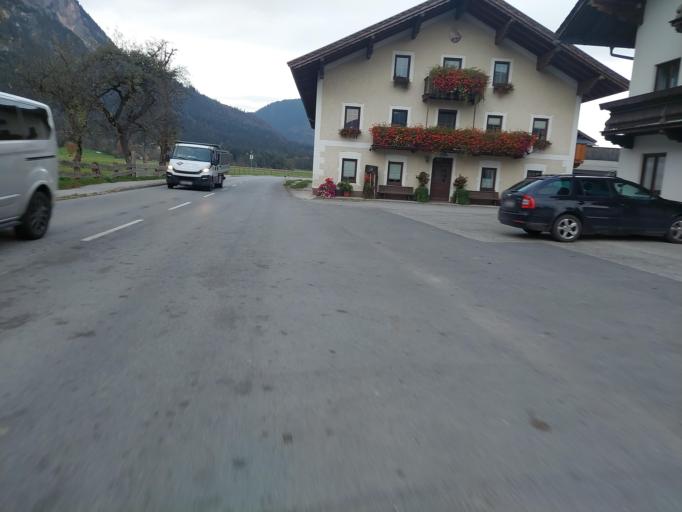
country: AT
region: Tyrol
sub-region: Politischer Bezirk Kufstein
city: Munster
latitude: 47.4266
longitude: 11.8416
